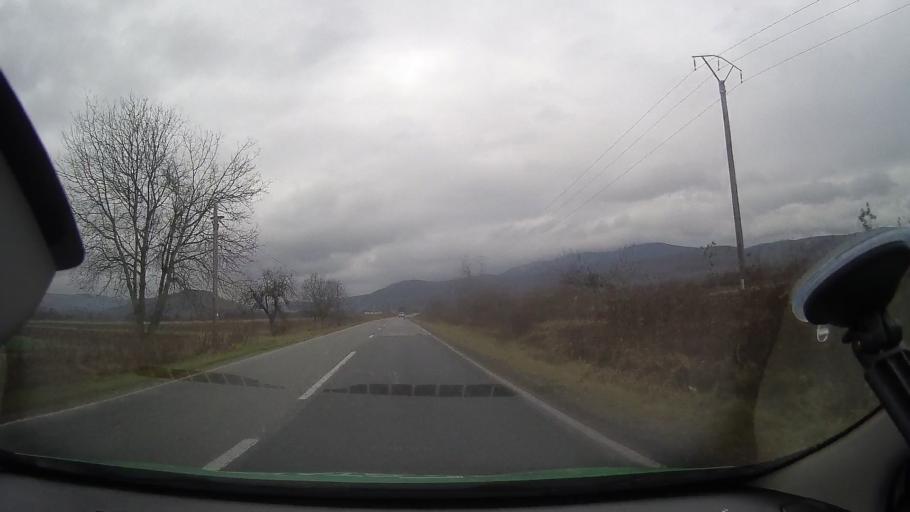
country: RO
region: Arad
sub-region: Comuna Buteni
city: Buteni
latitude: 46.3197
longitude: 22.1320
